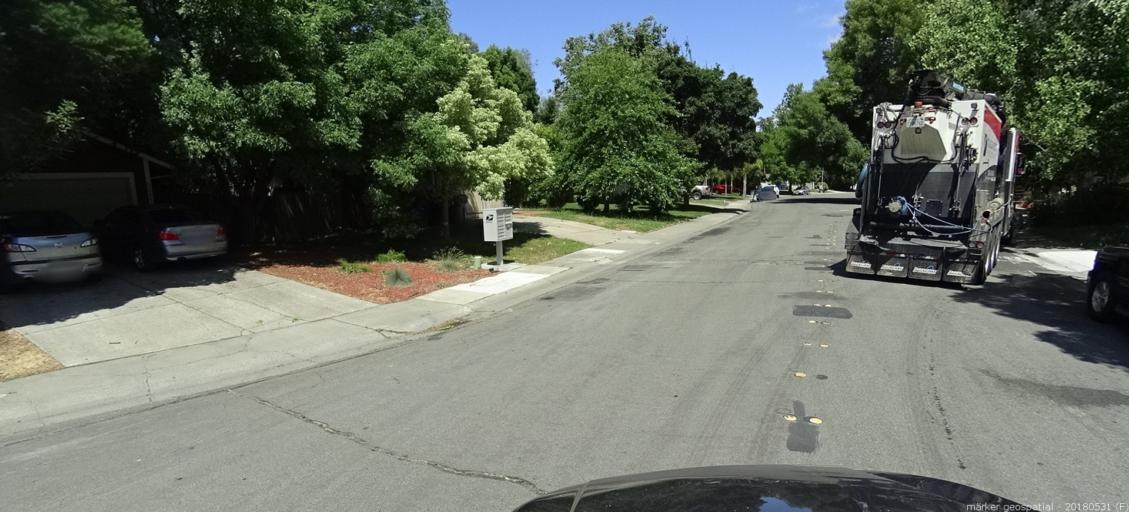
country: US
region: California
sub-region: Sacramento County
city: Sacramento
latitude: 38.6205
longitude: -121.5135
